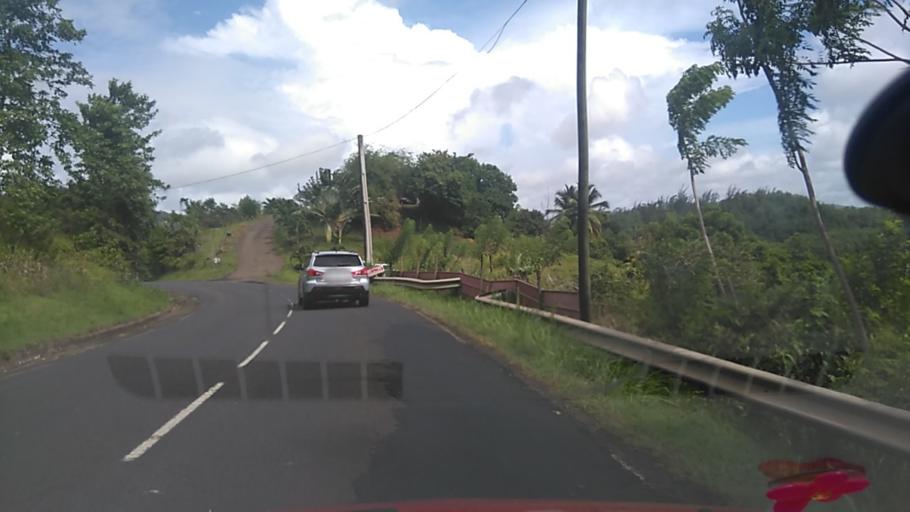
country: MQ
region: Martinique
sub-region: Martinique
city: Le Francois
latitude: 14.5973
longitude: -60.9261
